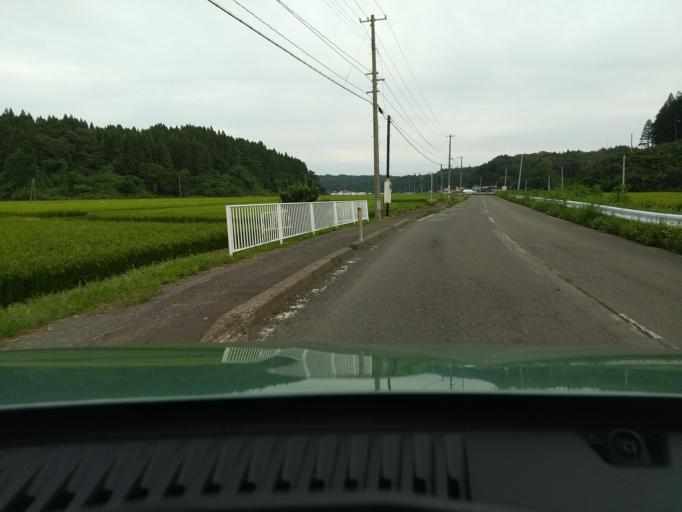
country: JP
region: Akita
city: Akita
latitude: 39.7883
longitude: 140.1204
